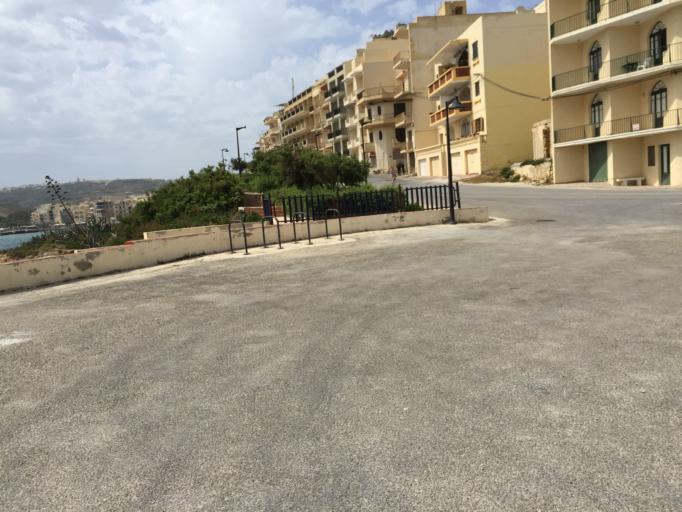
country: MT
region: Iz-Zebbug
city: Zebbug
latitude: 36.0758
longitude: 14.2579
